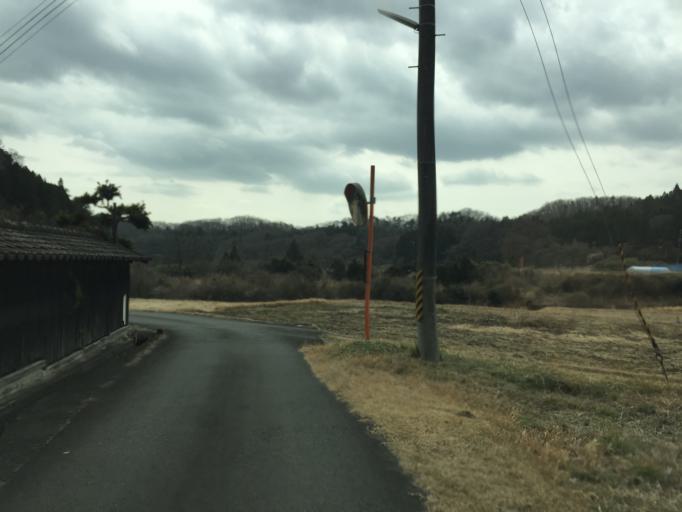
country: JP
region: Fukushima
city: Iwaki
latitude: 37.0023
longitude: 140.7960
